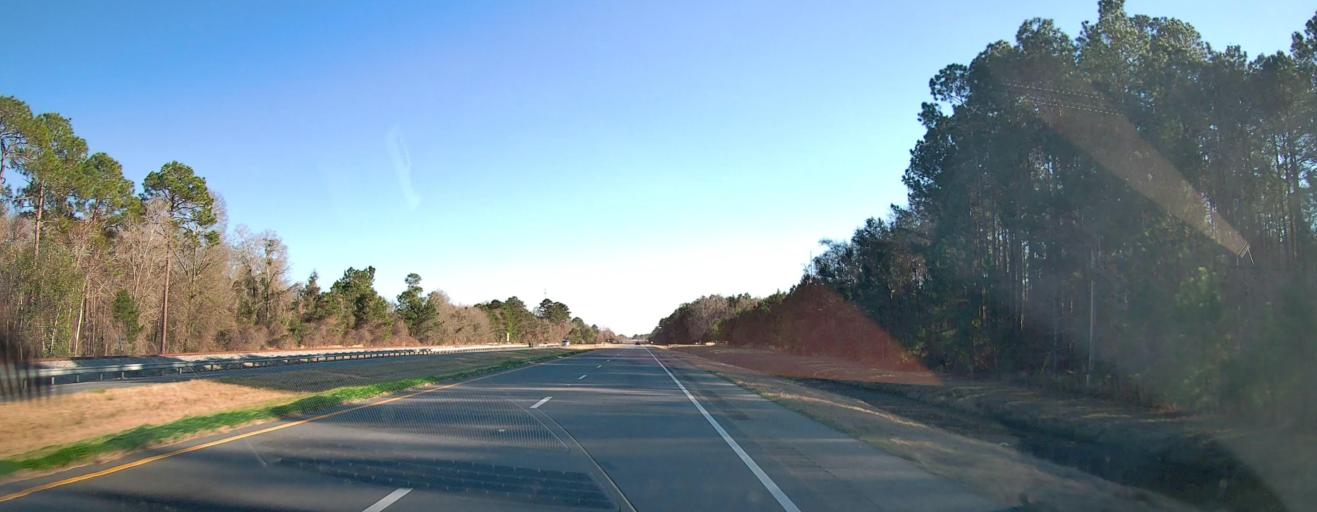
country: US
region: Georgia
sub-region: Lee County
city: Leesburg
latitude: 31.8379
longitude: -84.2224
